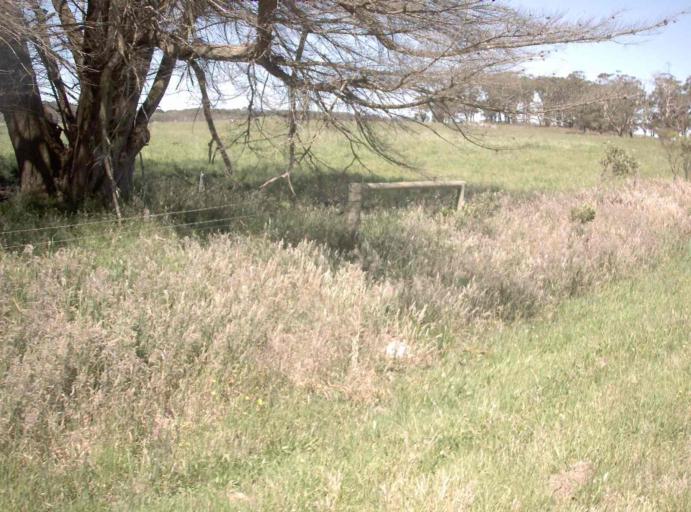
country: AU
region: Victoria
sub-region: Bass Coast
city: North Wonthaggi
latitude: -38.7452
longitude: 146.0736
